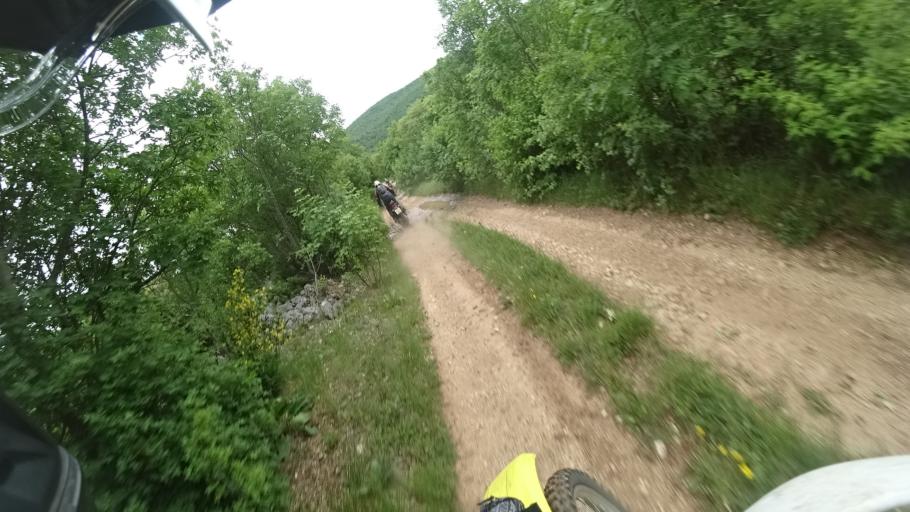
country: HR
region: Splitsko-Dalmatinska
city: Hrvace
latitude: 43.8933
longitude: 16.5311
